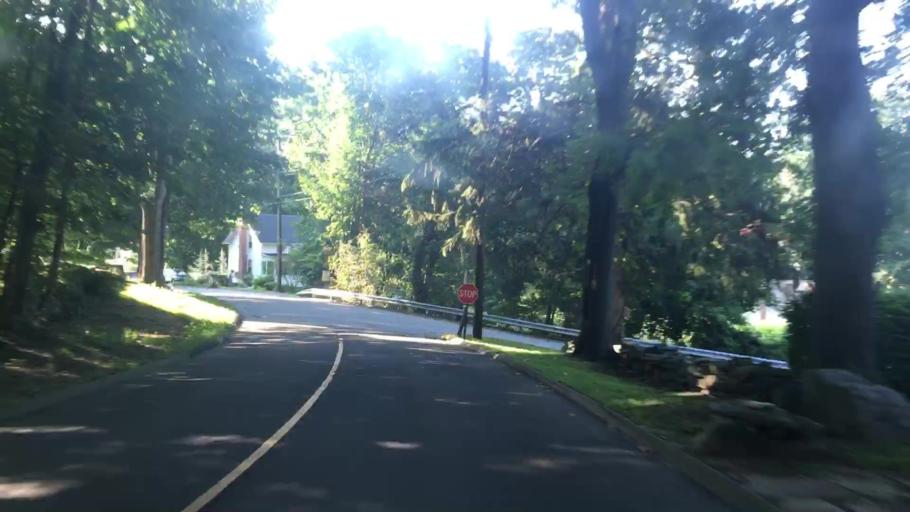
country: US
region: Connecticut
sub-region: Middlesex County
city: Chester Center
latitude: 41.3979
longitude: -72.4551
